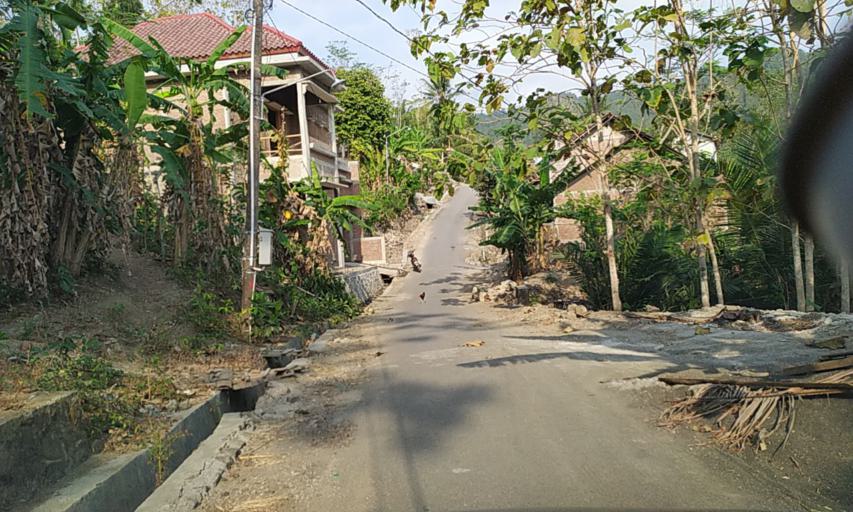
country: ID
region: Central Java
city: Sudikampir
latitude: -7.4878
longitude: 108.9471
